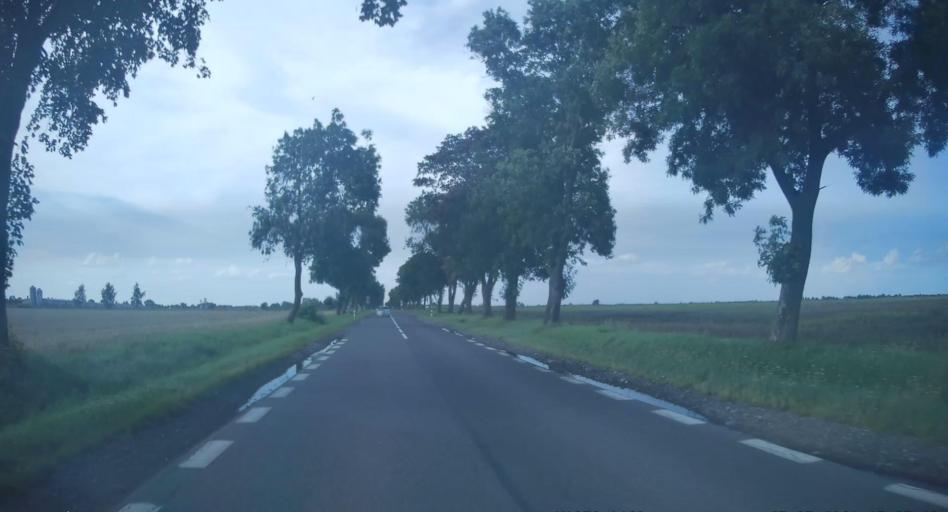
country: PL
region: Lodz Voivodeship
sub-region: Powiat tomaszowski
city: Rzeczyca
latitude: 51.6215
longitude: 20.2929
